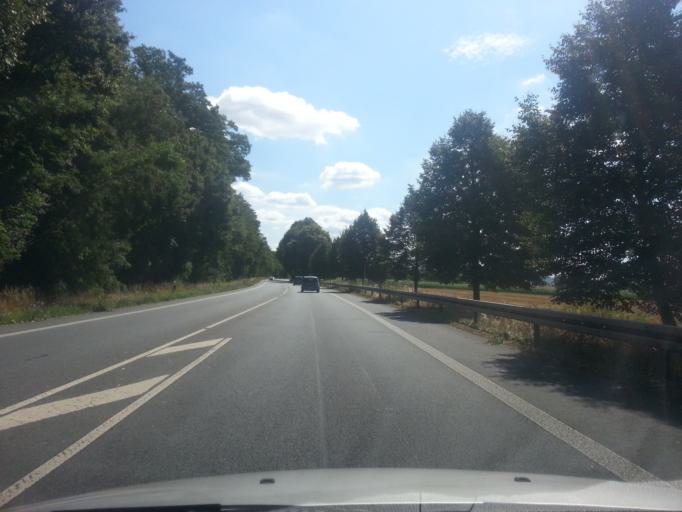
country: DE
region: Hesse
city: Dieburg
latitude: 49.8874
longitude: 8.8752
